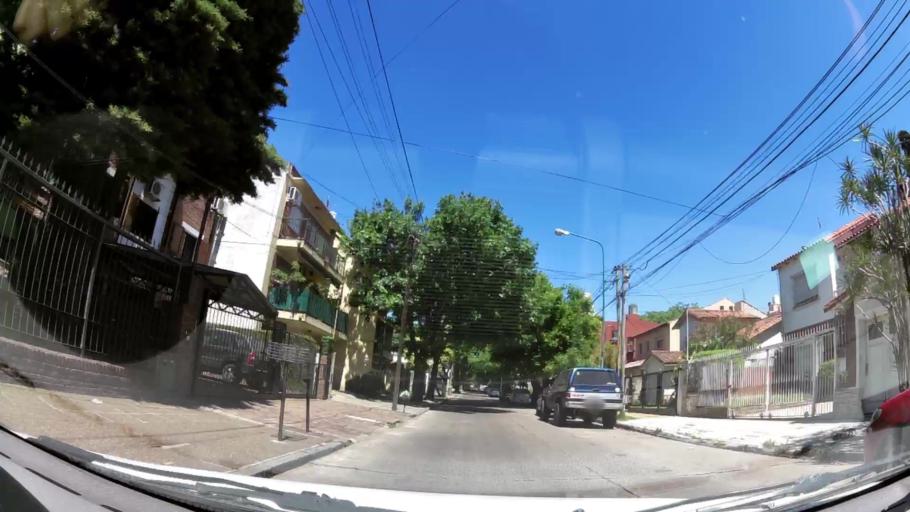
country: AR
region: Buenos Aires
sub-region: Partido de Vicente Lopez
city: Olivos
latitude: -34.5109
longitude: -58.4980
